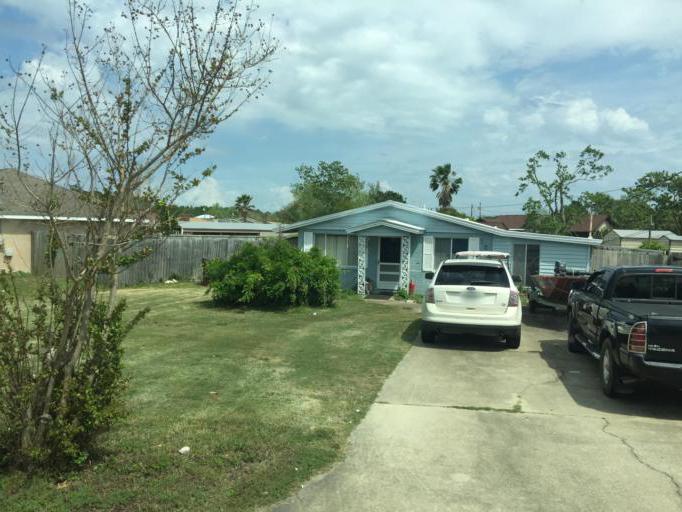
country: US
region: Florida
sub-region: Bay County
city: Laguna Beach
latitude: 30.2352
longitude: -85.8946
